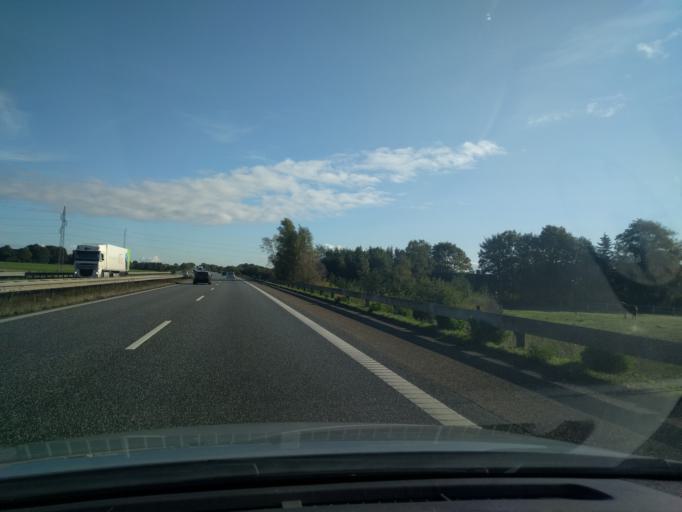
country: DK
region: Zealand
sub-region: Ringsted Kommune
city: Ringsted
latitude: 55.4500
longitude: 11.6947
